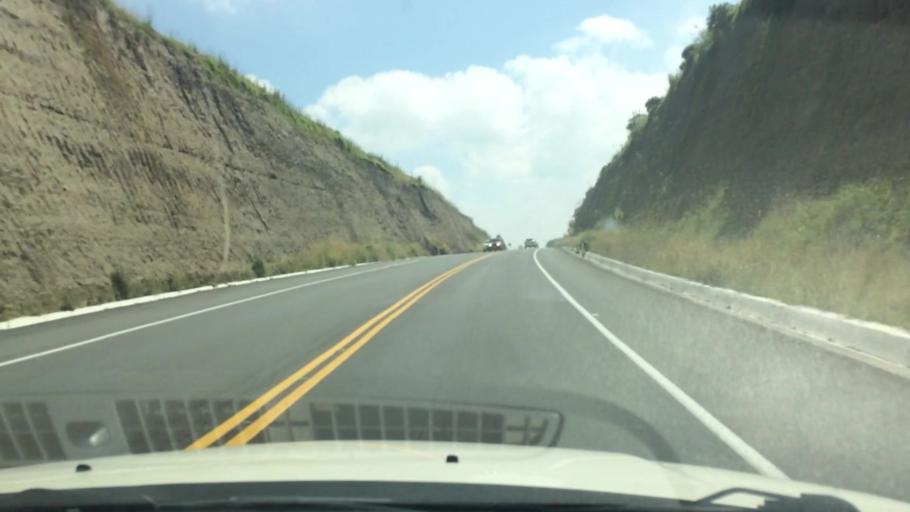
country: MX
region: Mexico
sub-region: Almoloya de Juarez
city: San Pedro de la Hortaliza (Ejido Almoloyan)
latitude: 19.3788
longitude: -99.8595
